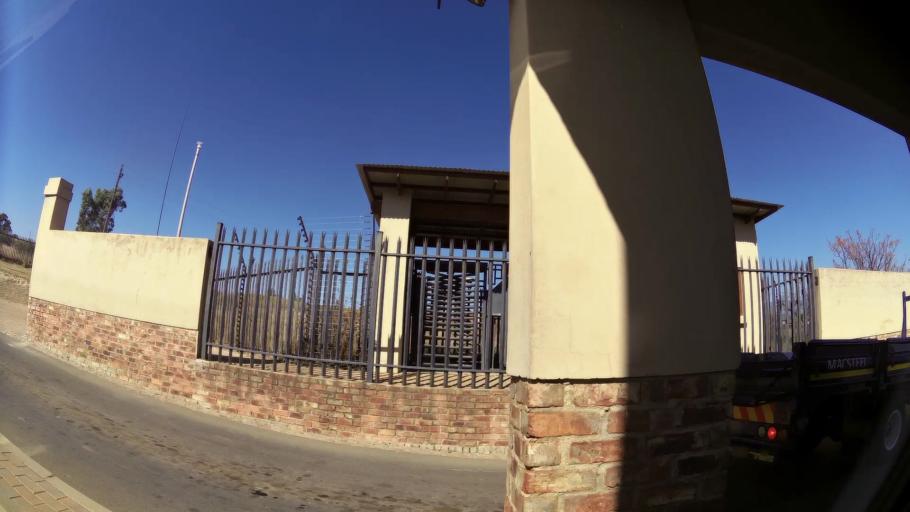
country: ZA
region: Gauteng
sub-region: City of Johannesburg Metropolitan Municipality
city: Midrand
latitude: -25.9507
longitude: 28.0821
